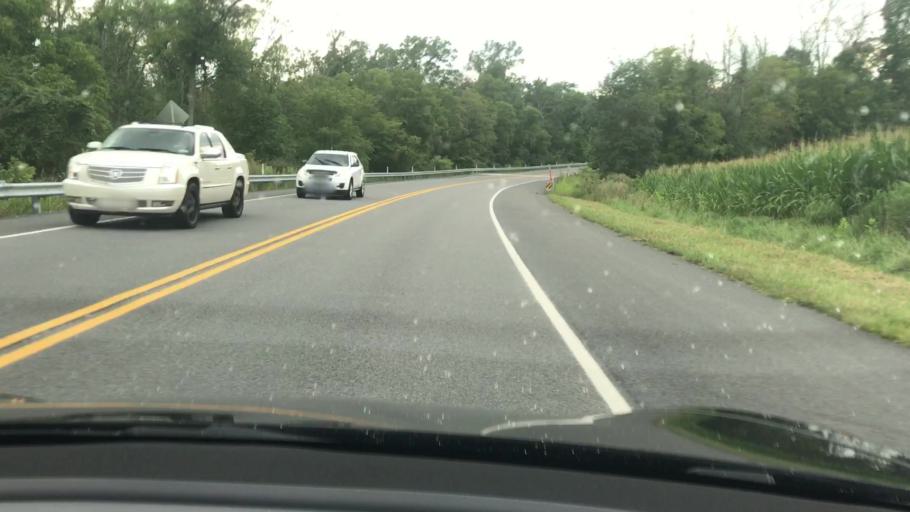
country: US
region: Pennsylvania
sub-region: York County
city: Valley Green
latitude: 40.1292
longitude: -76.8535
